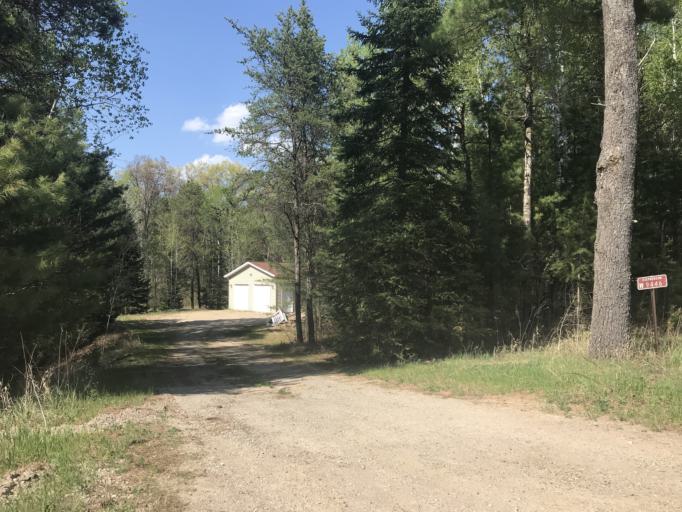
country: US
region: Wisconsin
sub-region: Marinette County
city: Peshtigo
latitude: 45.2498
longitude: -88.0707
